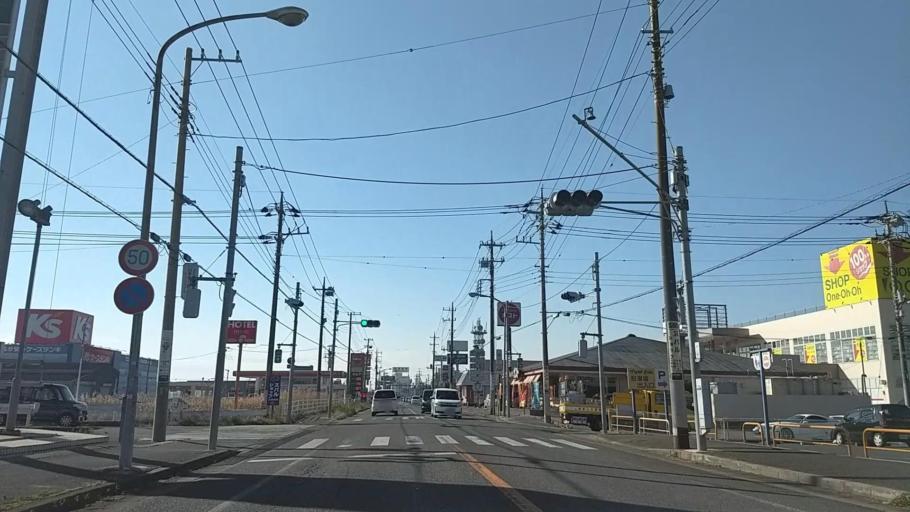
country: JP
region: Chiba
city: Yokaichiba
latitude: 35.7045
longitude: 140.5597
